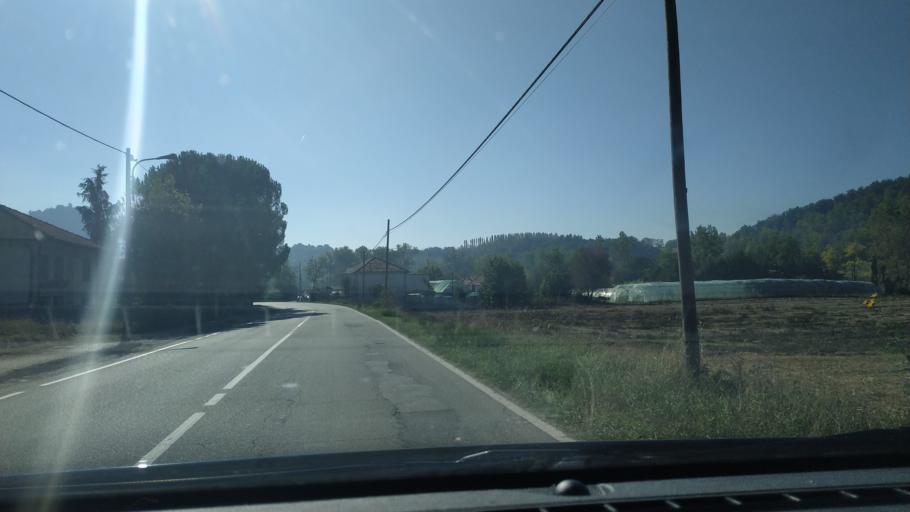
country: IT
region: Piedmont
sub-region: Provincia di Alessandria
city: Murisengo
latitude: 45.0836
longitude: 8.1520
